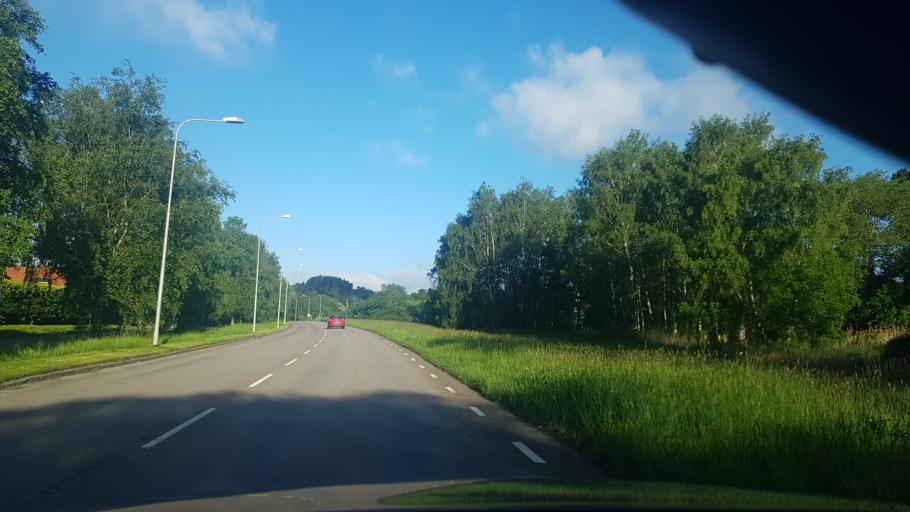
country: SE
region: Vaestra Goetaland
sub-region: Goteborg
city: Majorna
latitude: 57.6348
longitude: 11.8945
